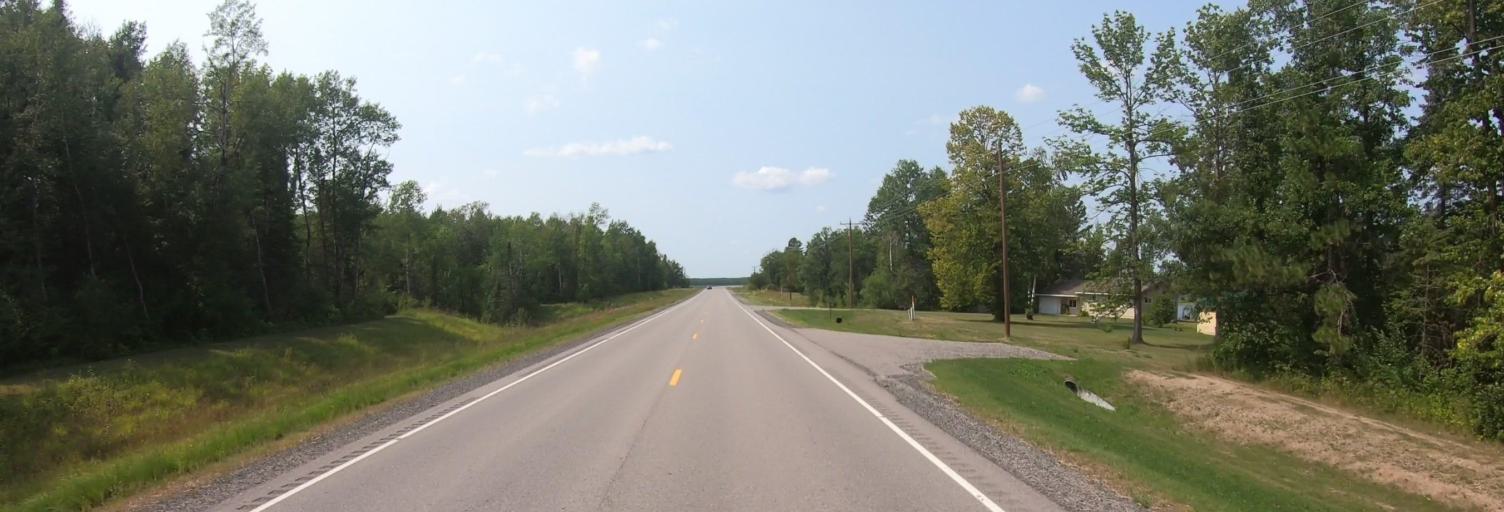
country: US
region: Minnesota
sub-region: Lake of the Woods County
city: Baudette
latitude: 48.6907
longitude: -94.4465
